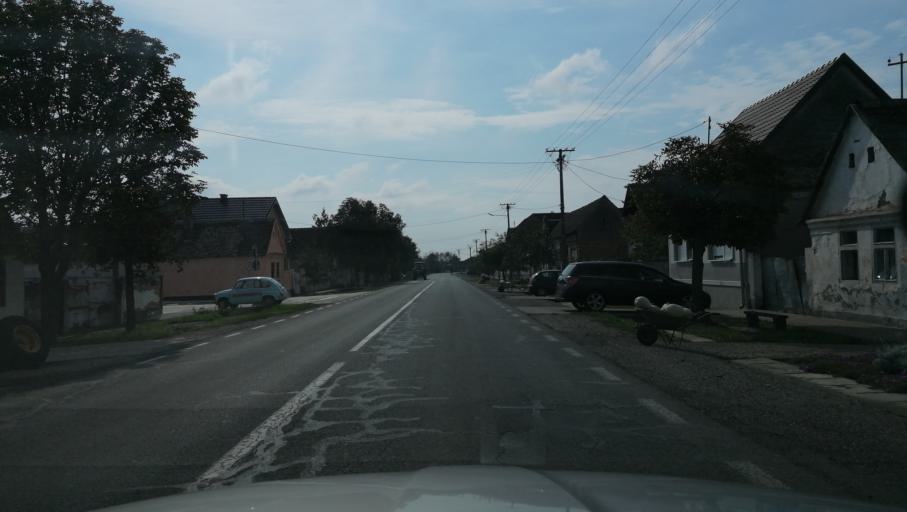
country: RS
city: Ravnje
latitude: 45.0174
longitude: 19.4002
